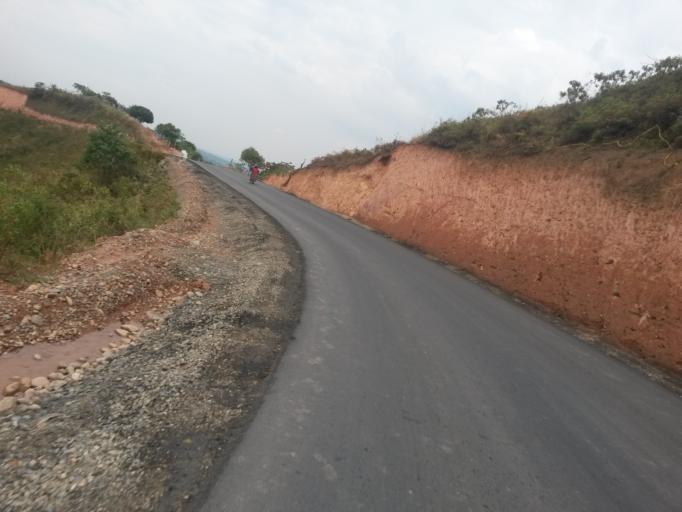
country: CO
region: Cauca
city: Buenos Aires
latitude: 3.0531
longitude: -76.6318
